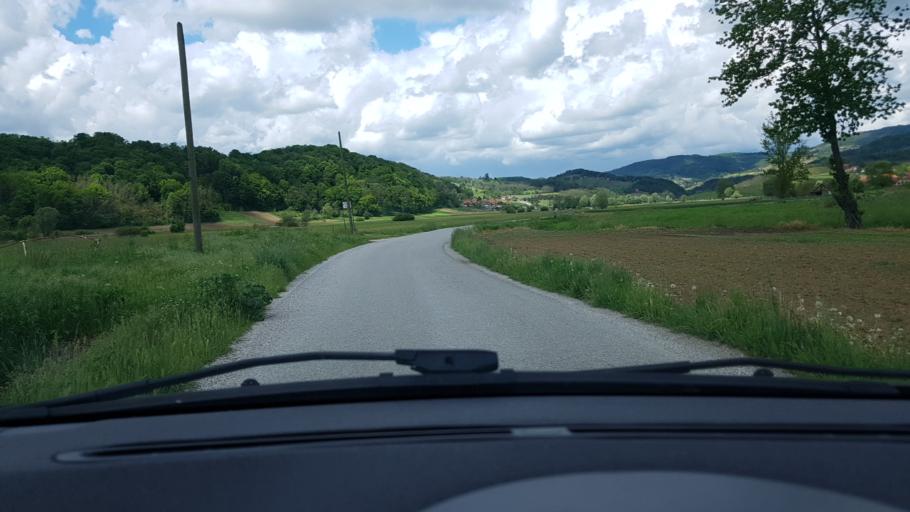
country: HR
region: Krapinsko-Zagorska
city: Pregrada
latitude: 46.1470
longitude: 15.8074
